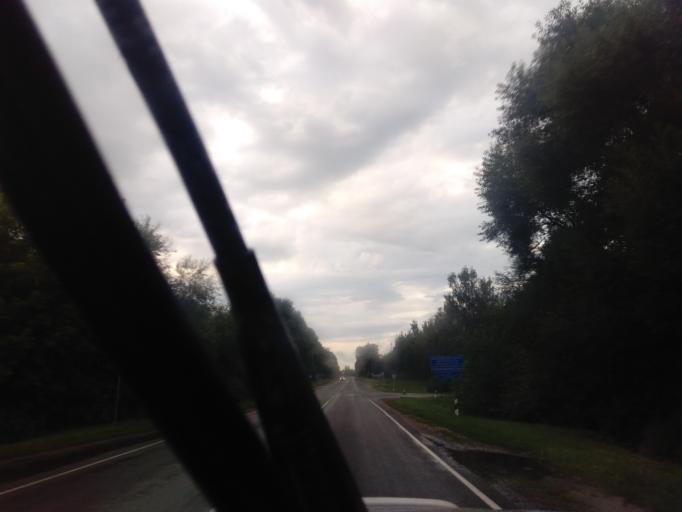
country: BY
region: Minsk
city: Enyerhyetykaw
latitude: 53.5786
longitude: 27.0573
